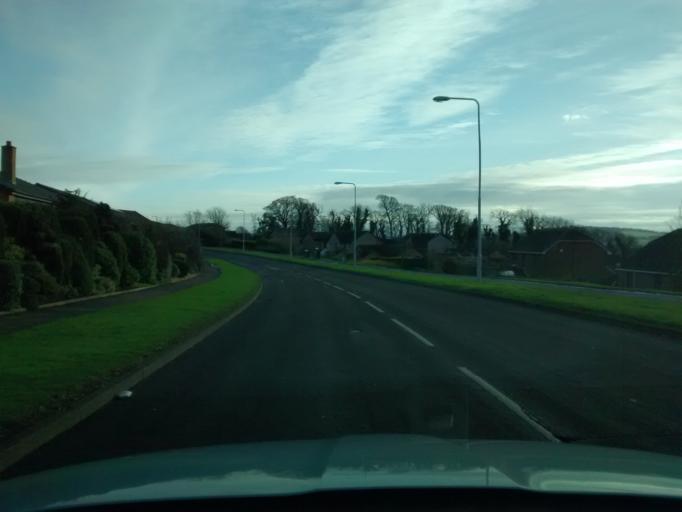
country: GB
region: Scotland
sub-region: Fife
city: Inverkeithing
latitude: 56.0301
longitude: -3.3643
